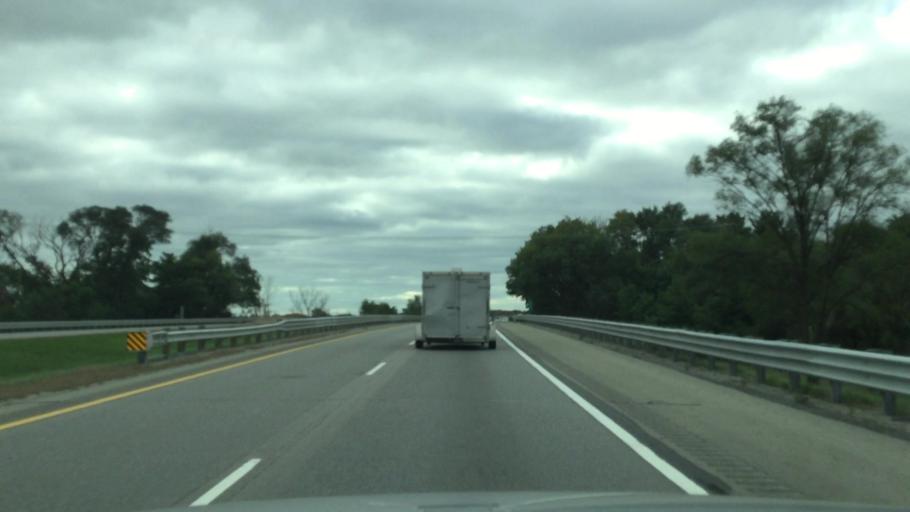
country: US
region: Michigan
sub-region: Macomb County
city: Shelby
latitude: 42.6854
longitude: -83.0169
